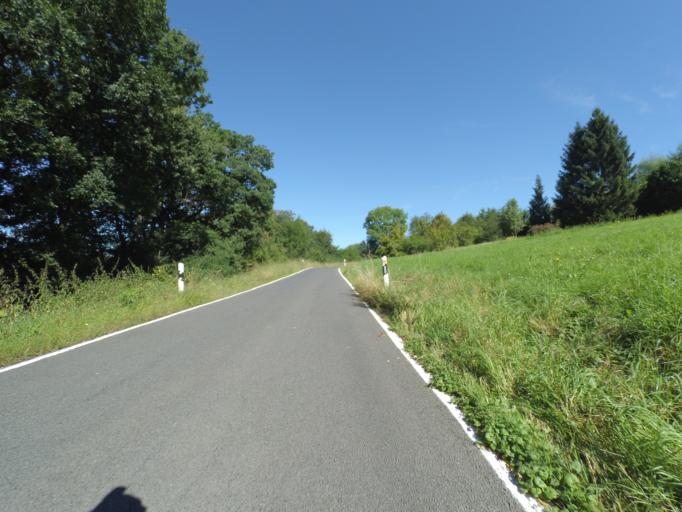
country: DE
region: Rheinland-Pfalz
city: Plein
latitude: 50.0362
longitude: 6.8604
